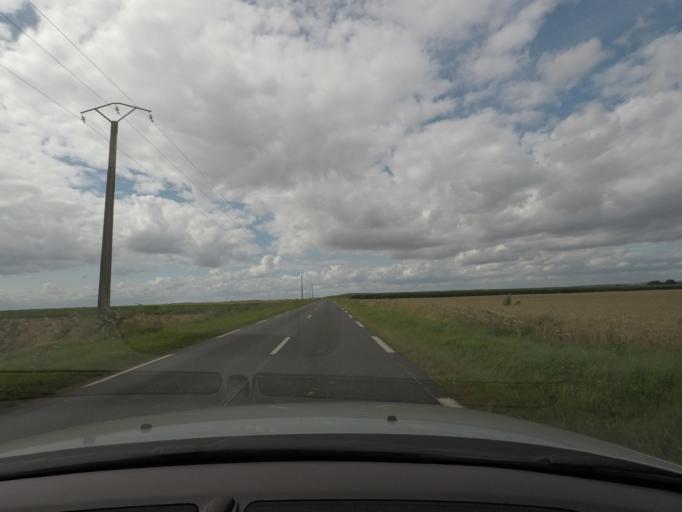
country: FR
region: Haute-Normandie
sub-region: Departement de l'Eure
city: Les Andelys
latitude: 49.2109
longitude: 1.4607
